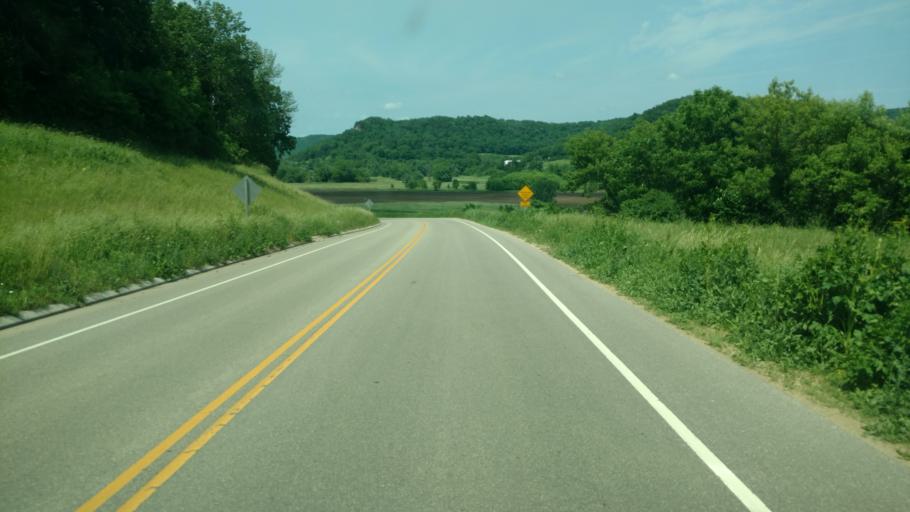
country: US
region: Wisconsin
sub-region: Vernon County
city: Viroqua
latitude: 43.5114
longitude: -90.6593
